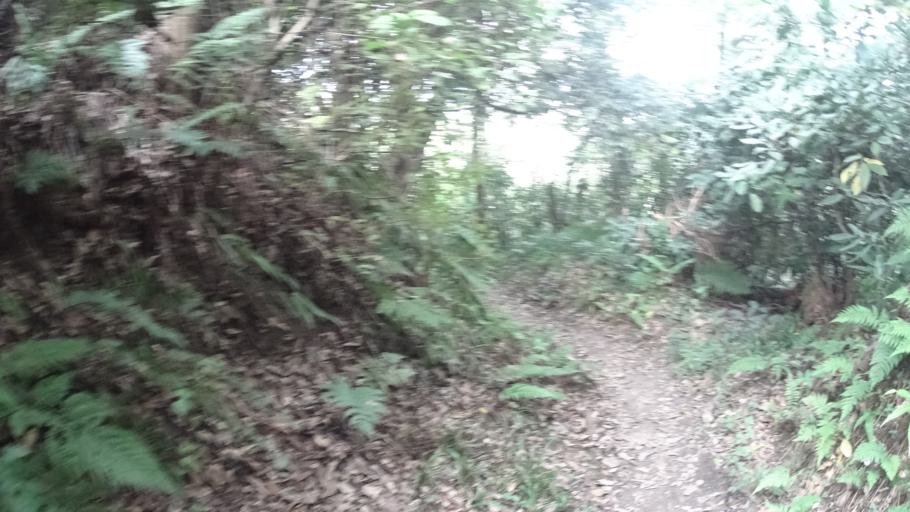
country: JP
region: Kanagawa
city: Zushi
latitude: 35.2918
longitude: 139.6050
